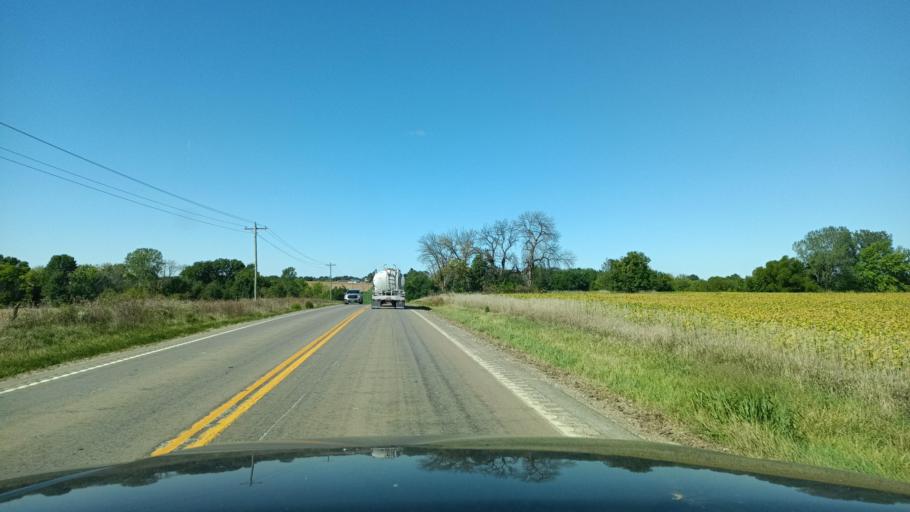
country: US
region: Missouri
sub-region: Scotland County
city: Memphis
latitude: 40.4549
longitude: -92.0409
